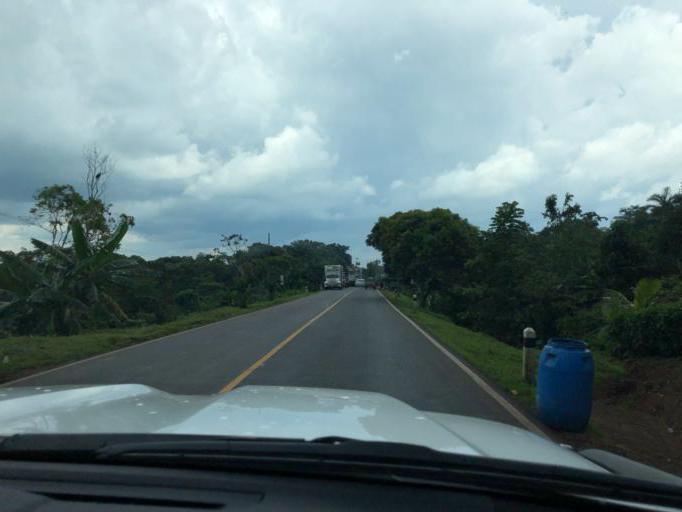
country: NI
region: Chontales
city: Villa Sandino
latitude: 11.9973
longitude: -84.7847
